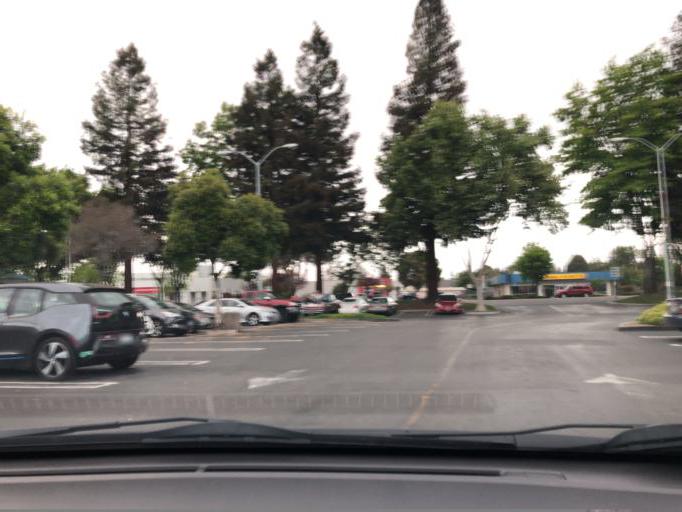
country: US
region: California
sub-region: Santa Clara County
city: Mountain View
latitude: 37.3788
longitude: -122.0710
